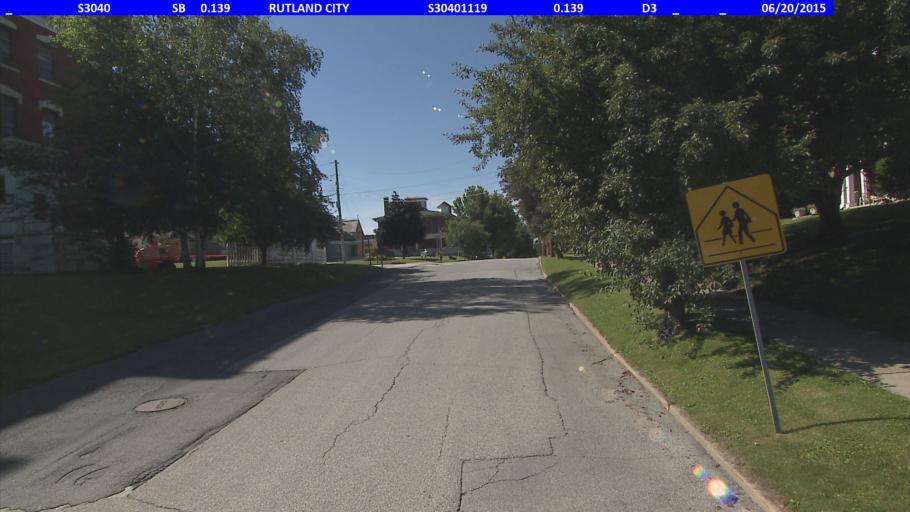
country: US
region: Vermont
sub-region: Rutland County
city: Rutland
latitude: 43.6032
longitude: -72.9864
